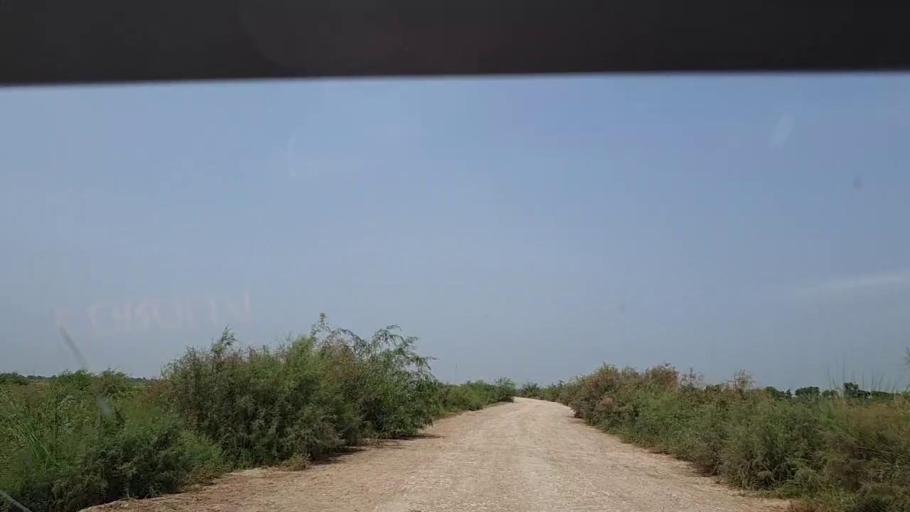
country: PK
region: Sindh
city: Adilpur
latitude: 27.9061
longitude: 69.2229
